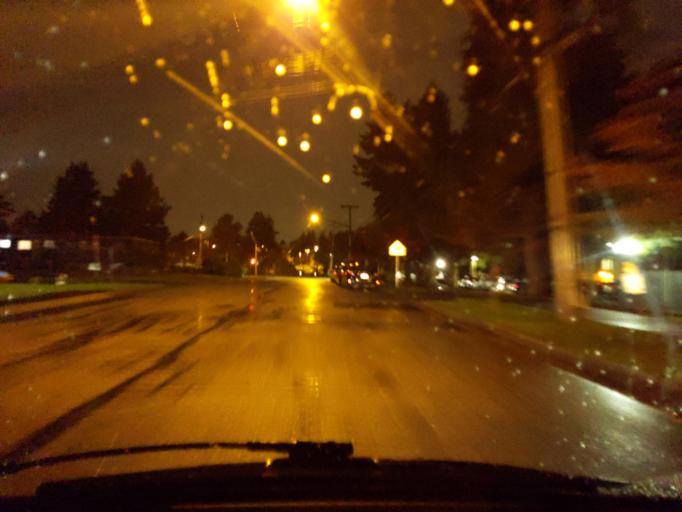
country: CA
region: British Columbia
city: New Westminster
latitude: 49.1933
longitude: -122.8550
